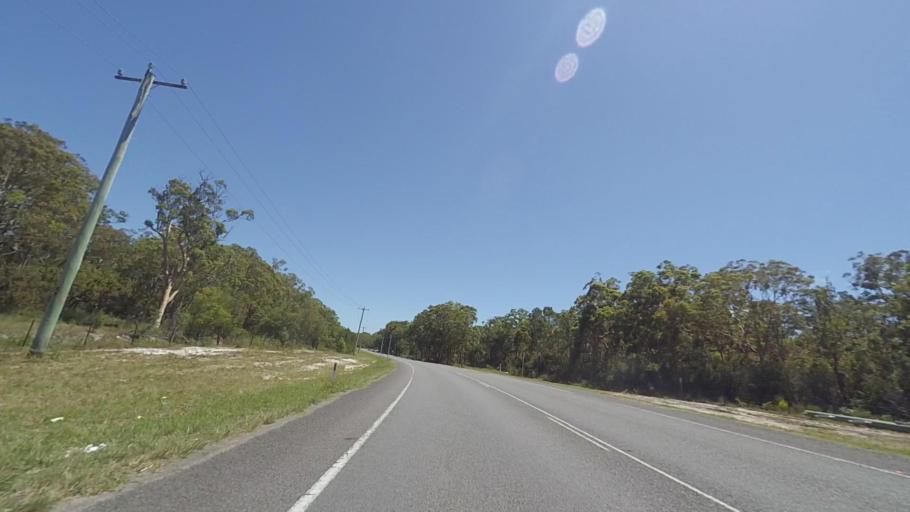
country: AU
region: New South Wales
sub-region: Port Stephens Shire
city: Medowie
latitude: -32.7798
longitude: 151.8592
